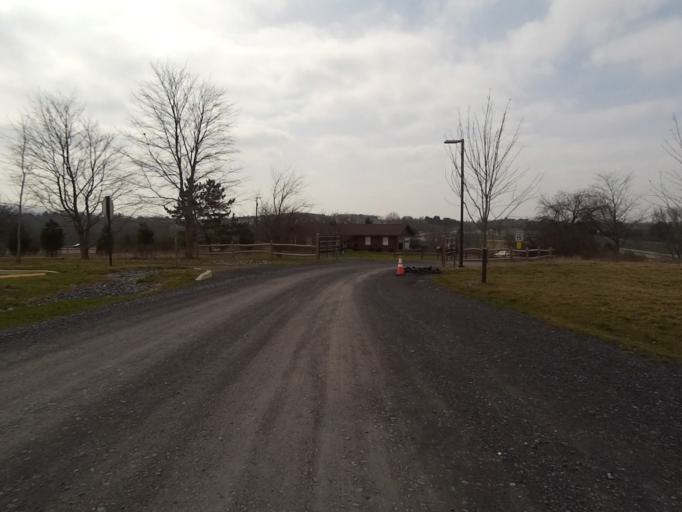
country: US
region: Pennsylvania
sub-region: Centre County
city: Boalsburg
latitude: 40.7904
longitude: -77.7959
